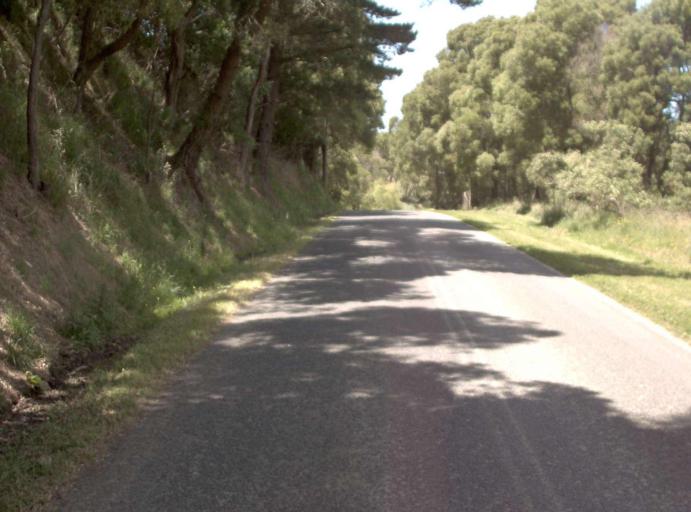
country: AU
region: Victoria
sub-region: Bass Coast
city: North Wonthaggi
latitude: -38.7193
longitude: 146.1194
